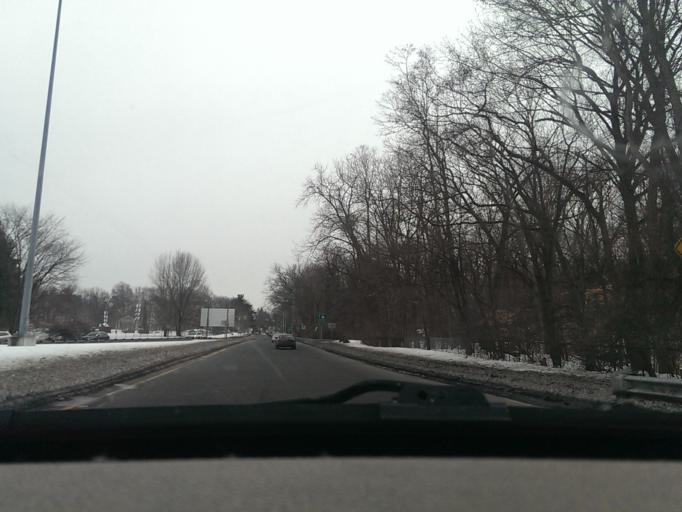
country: US
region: Massachusetts
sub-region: Hampden County
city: Longmeadow
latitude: 42.0740
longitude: -72.5832
